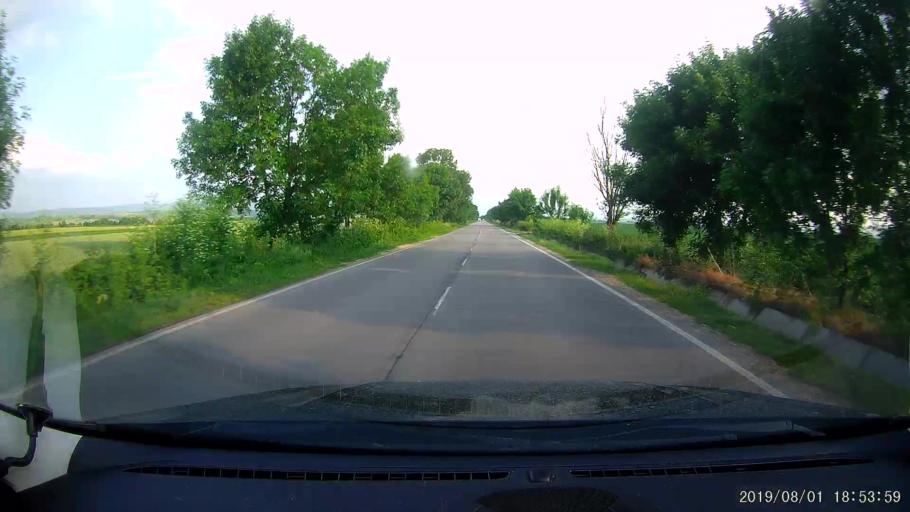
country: BG
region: Shumen
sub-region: Obshtina Shumen
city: Shumen
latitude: 43.2099
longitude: 26.9988
